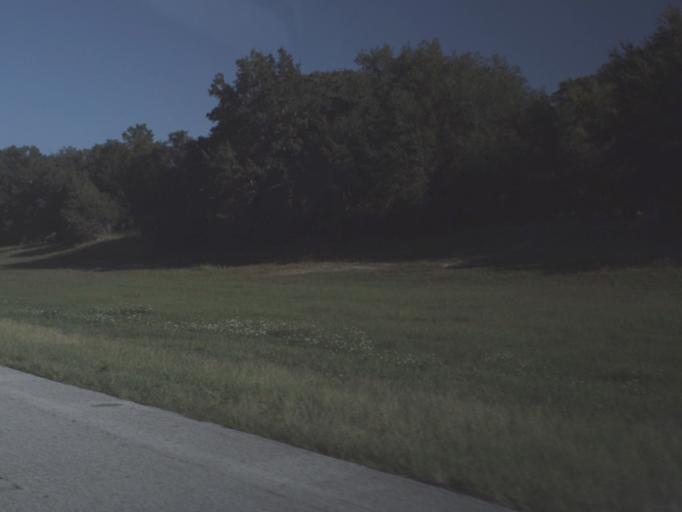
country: US
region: Florida
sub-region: Lake County
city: Hawthorne
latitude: 28.7197
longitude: -81.9010
